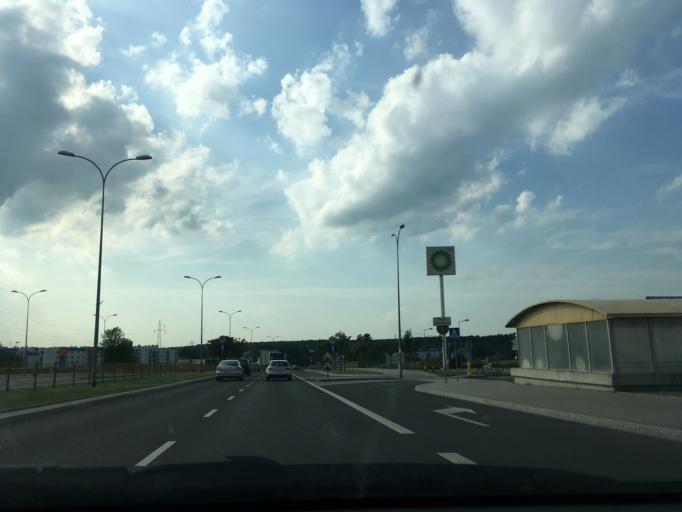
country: PL
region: Podlasie
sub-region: Bialystok
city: Bialystok
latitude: 53.1541
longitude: 23.1614
